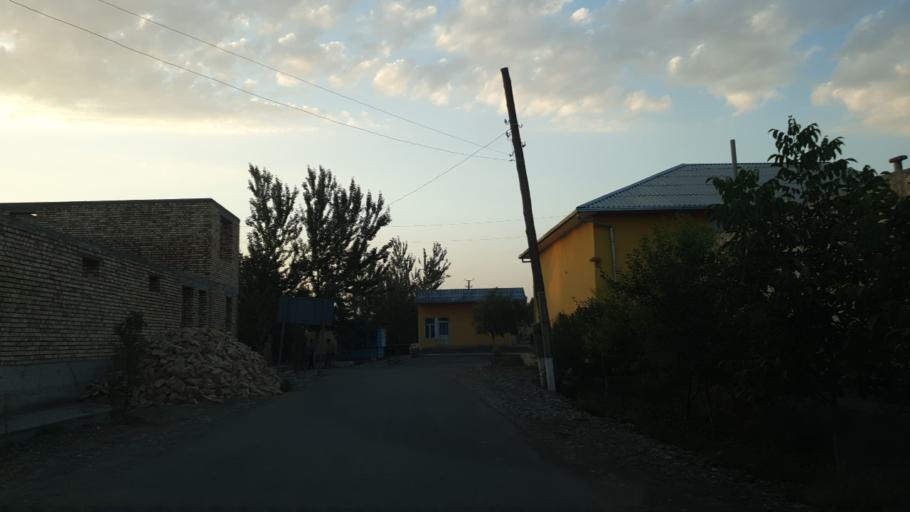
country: UZ
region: Fergana
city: Beshariq
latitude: 40.4962
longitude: 70.6207
